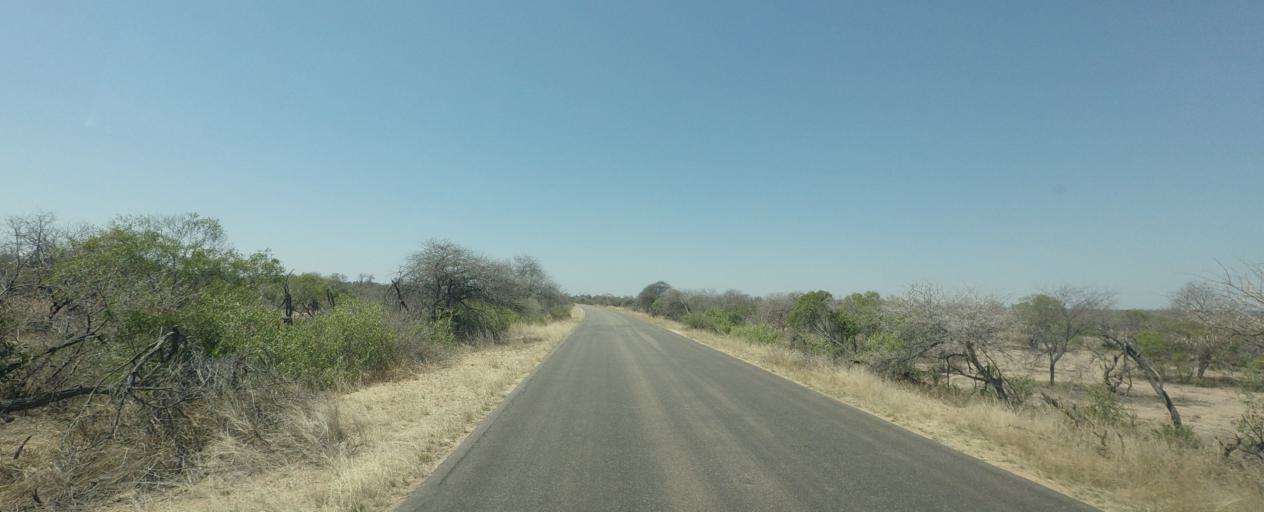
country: ZA
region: Limpopo
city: Thulamahashi
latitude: -24.4358
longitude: 31.4952
